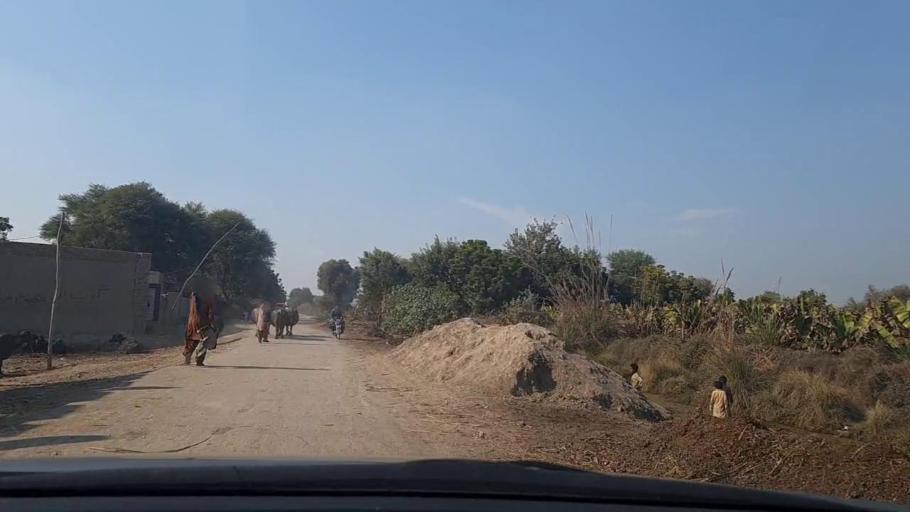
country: PK
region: Sindh
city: Daulatpur
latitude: 26.3053
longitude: 68.0881
